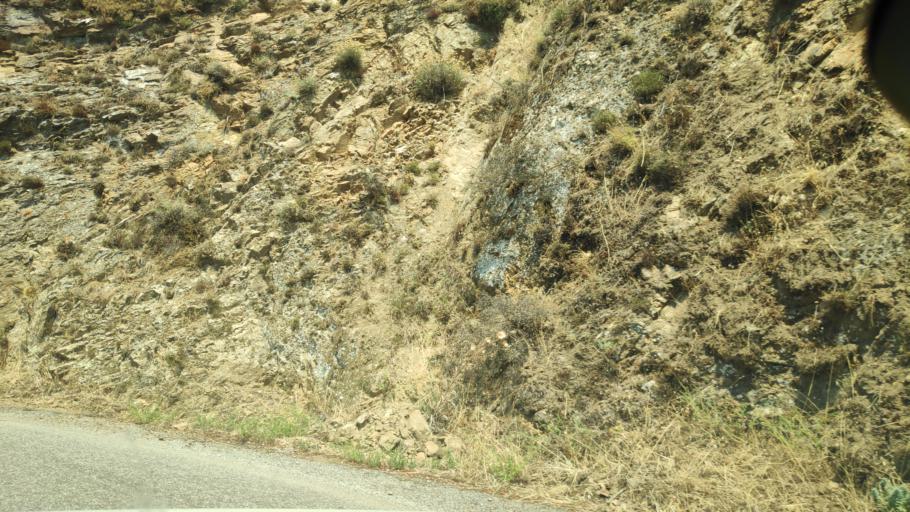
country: IT
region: Calabria
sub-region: Provincia di Reggio Calabria
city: Bova
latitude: 38.0039
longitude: 15.9320
